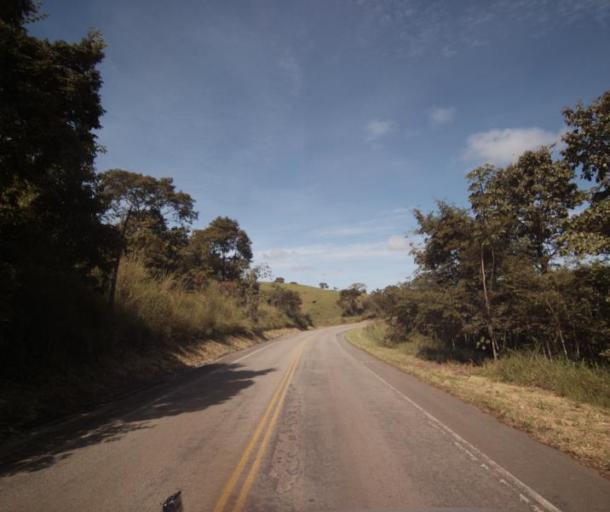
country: BR
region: Goias
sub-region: Abadiania
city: Abadiania
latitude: -16.1144
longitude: -48.8866
